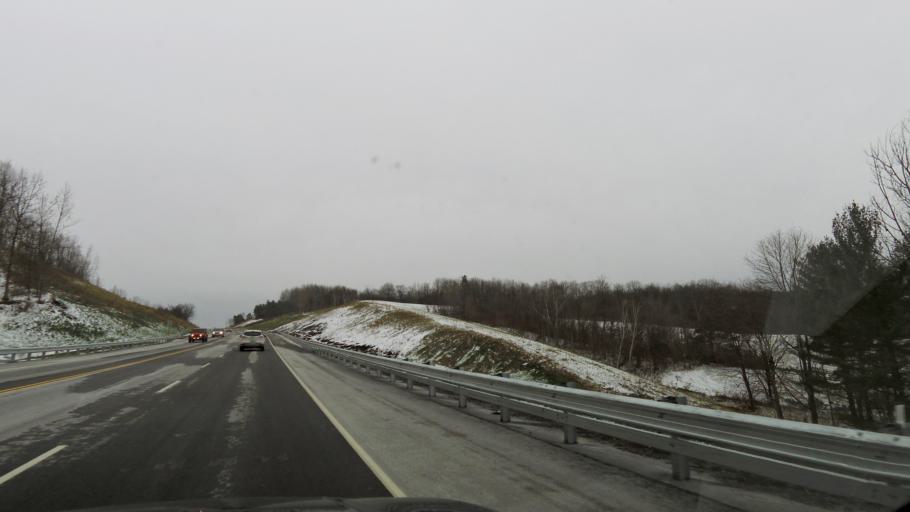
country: CA
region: Ontario
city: Newmarket
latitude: 44.0878
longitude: -79.5165
